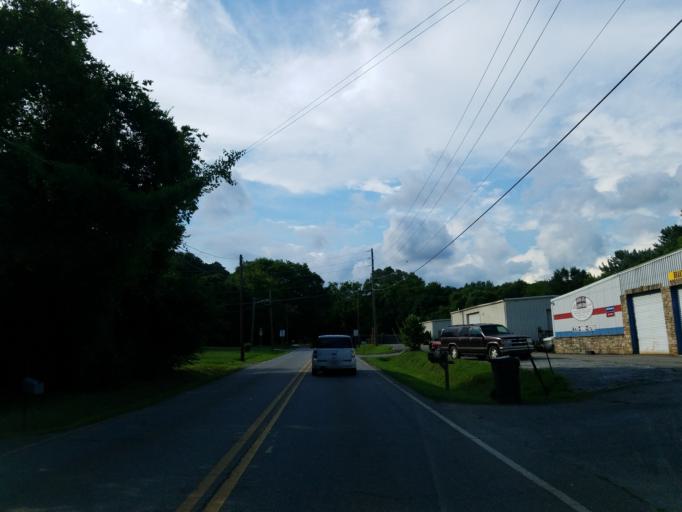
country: US
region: Georgia
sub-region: Bartow County
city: Emerson
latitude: 34.1285
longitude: -84.7571
